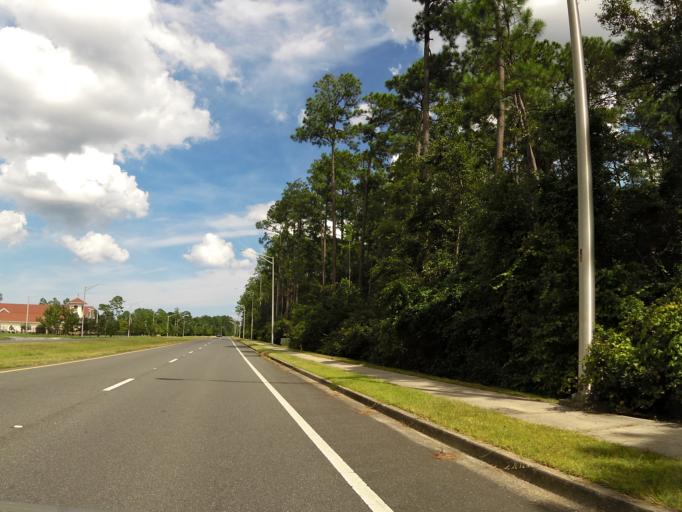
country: US
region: Florida
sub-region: Duval County
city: Jacksonville
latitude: 30.4757
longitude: -81.6194
